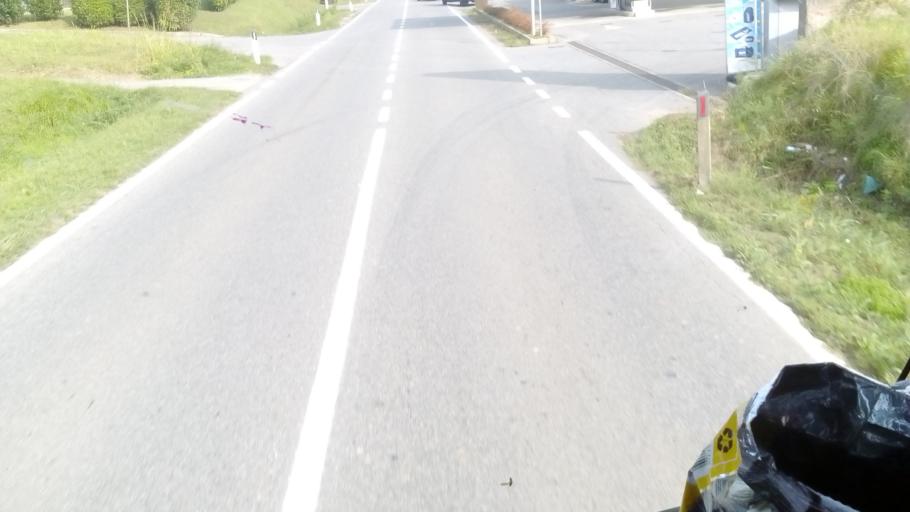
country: IT
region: Lombardy
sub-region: Provincia di Como
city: San Michele-San Giorgio
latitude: 45.6853
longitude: 9.0545
